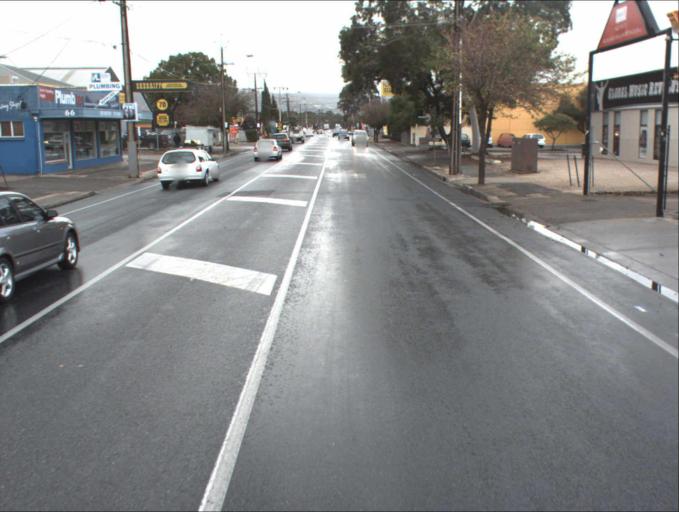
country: AU
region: South Australia
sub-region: Port Adelaide Enfield
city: Klemzig
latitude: -34.8803
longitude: 138.6357
